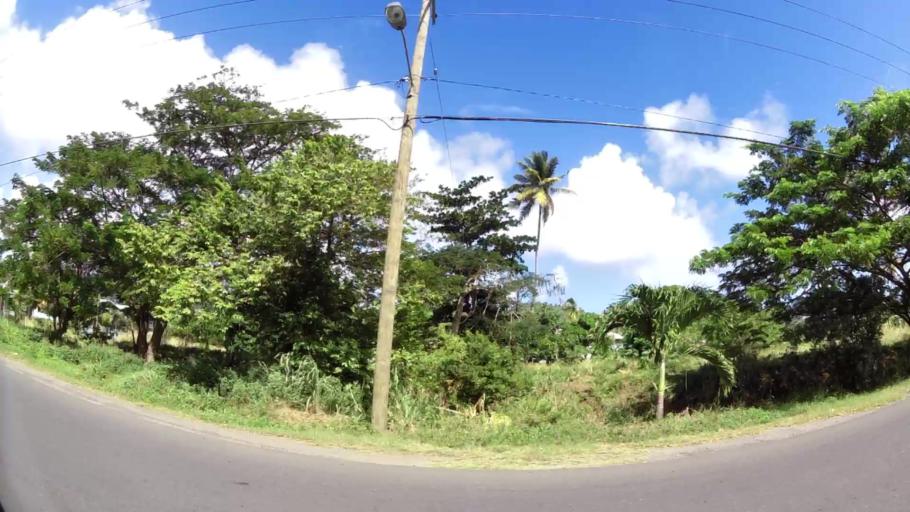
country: LC
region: Dennery Quarter
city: Dennery
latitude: 13.9305
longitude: -60.9023
